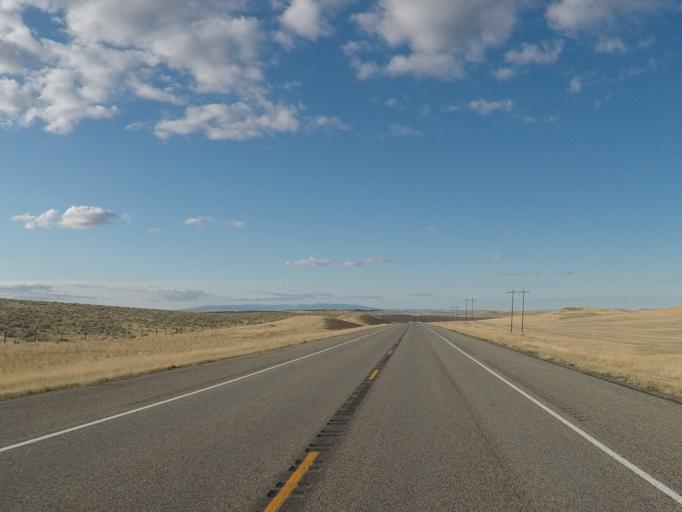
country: US
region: Montana
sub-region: Golden Valley County
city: Ryegate
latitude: 46.1826
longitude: -108.9110
